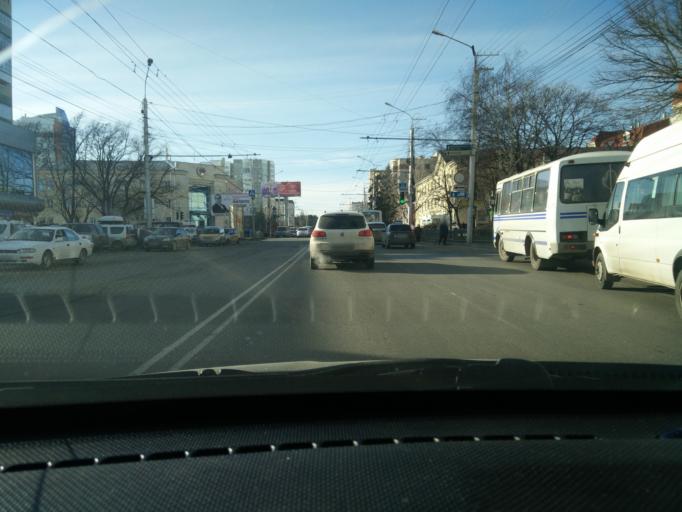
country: RU
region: Stavropol'skiy
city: Stavropol'
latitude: 45.0377
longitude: 41.9716
